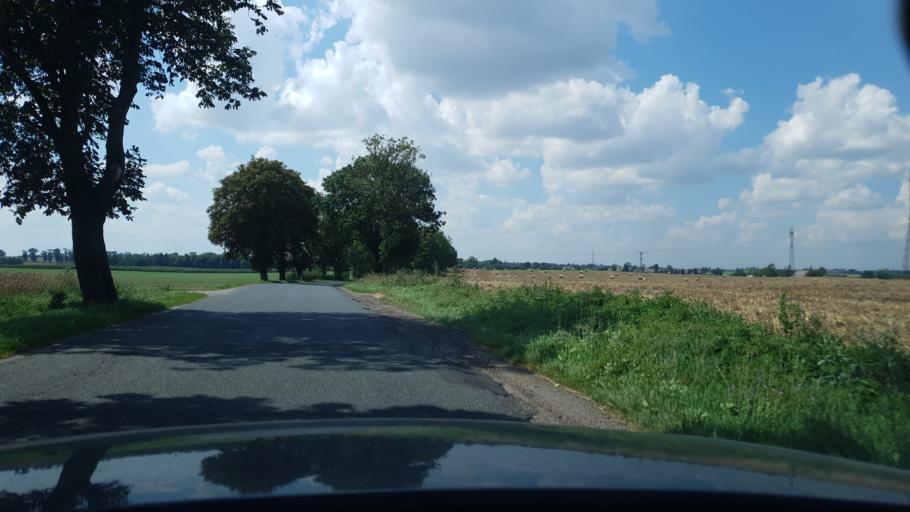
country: PL
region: Kujawsko-Pomorskie
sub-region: Powiat wabrzeski
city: Pluznica
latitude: 53.3729
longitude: 18.8185
